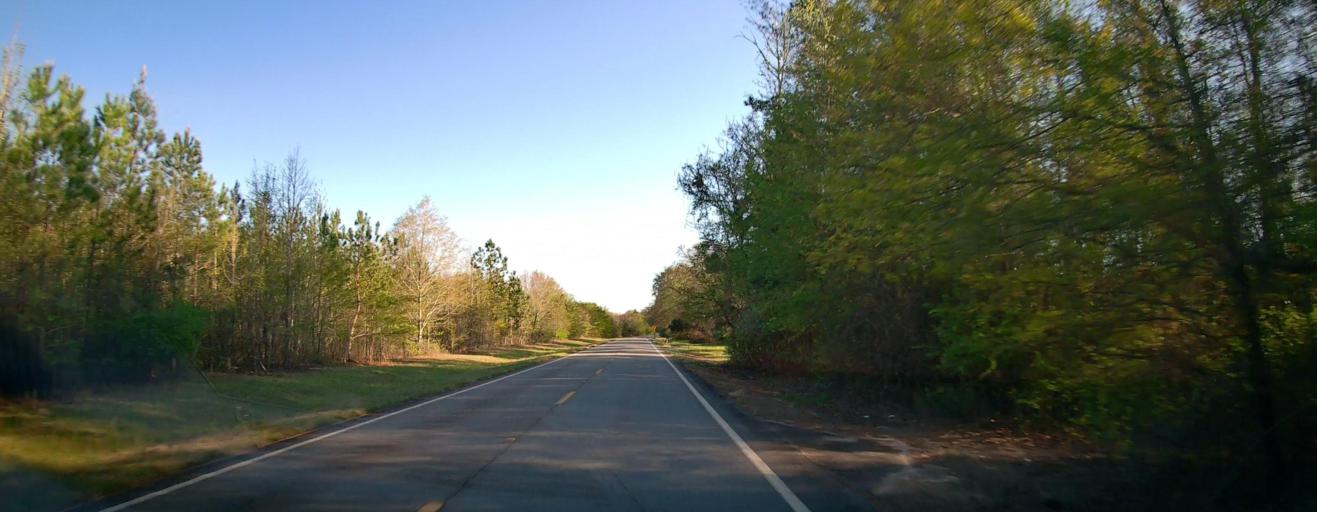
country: US
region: Georgia
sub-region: Wilkinson County
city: Irwinton
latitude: 32.9062
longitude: -83.1213
